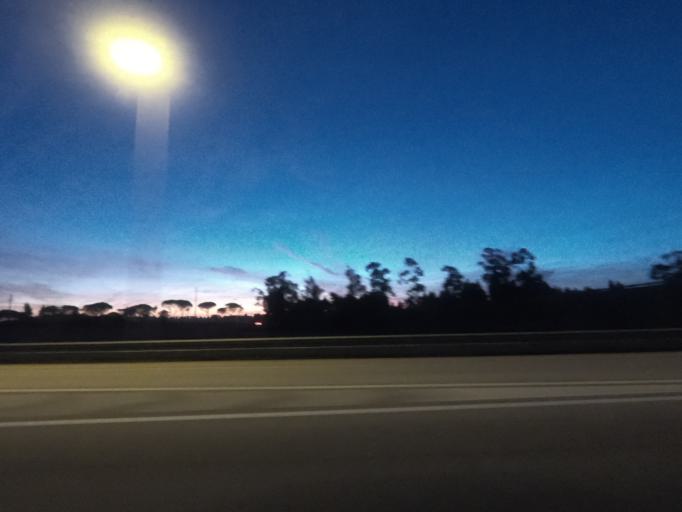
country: PT
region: Santarem
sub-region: Benavente
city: Benavente
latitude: 38.9601
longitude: -8.8323
